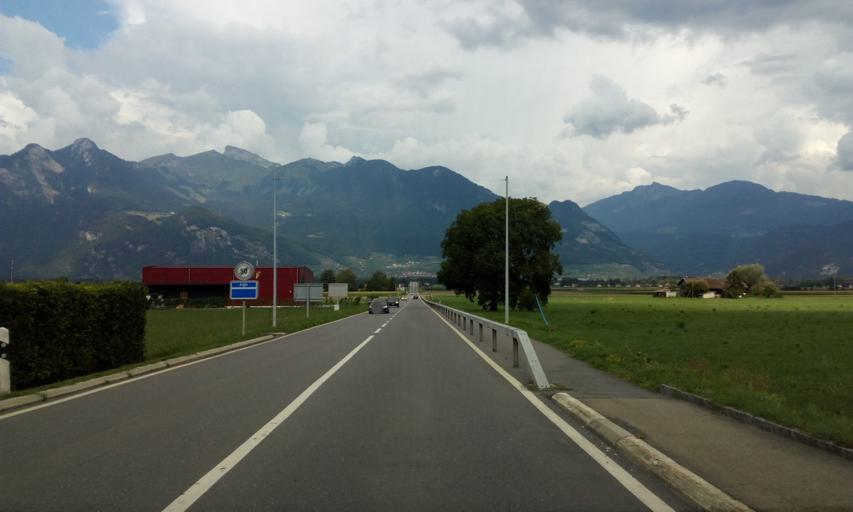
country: CH
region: Valais
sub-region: Monthey District
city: Vionnaz
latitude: 46.3114
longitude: 6.9059
